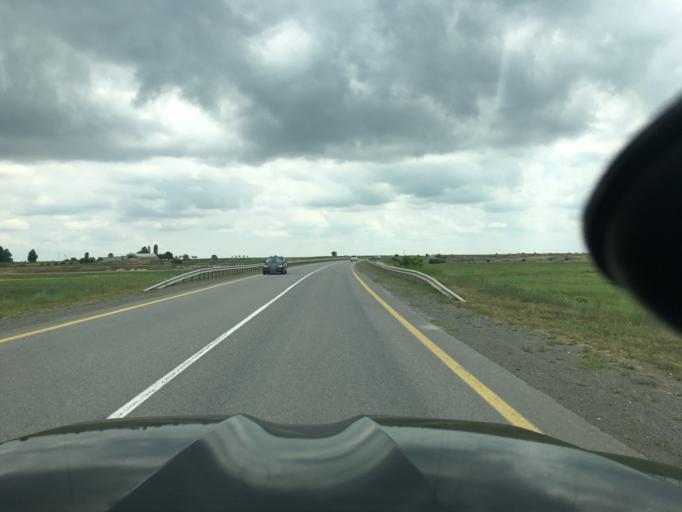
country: AZ
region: Tovuz
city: Qaraxanli
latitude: 41.0284
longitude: 45.6203
